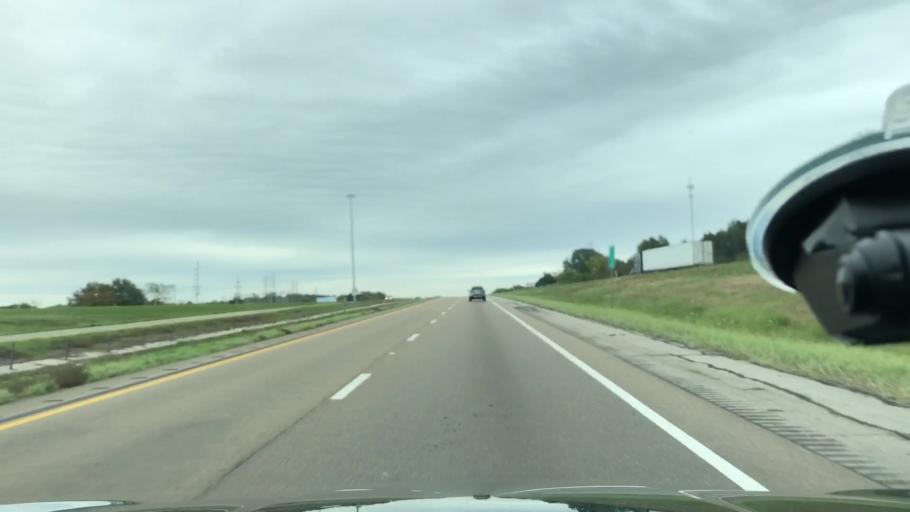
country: US
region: Texas
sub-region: Franklin County
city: Mount Vernon
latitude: 33.1601
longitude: -95.1124
